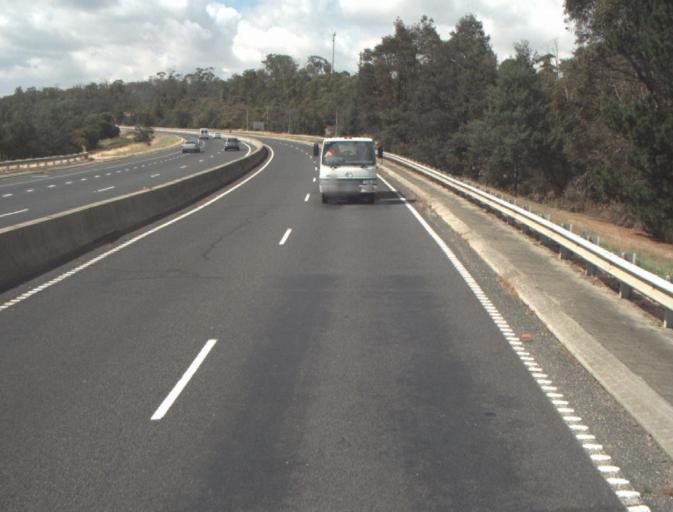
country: AU
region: Tasmania
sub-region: Launceston
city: Summerhill
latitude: -41.4720
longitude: 147.1426
